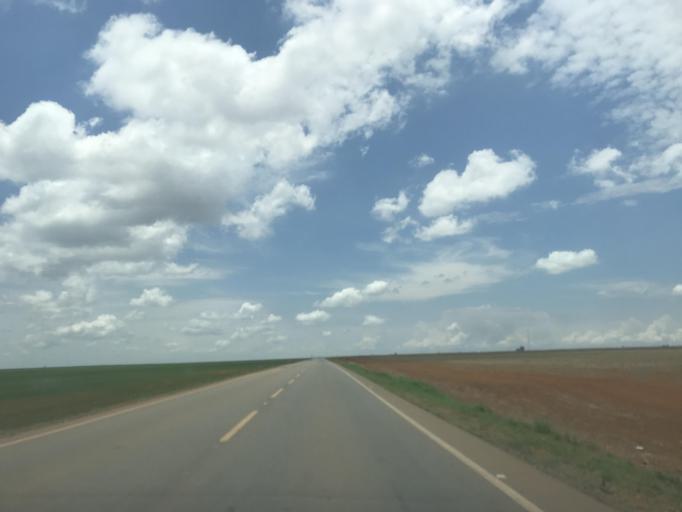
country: BR
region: Goias
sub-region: Vianopolis
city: Vianopolis
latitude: -16.5225
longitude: -48.2386
